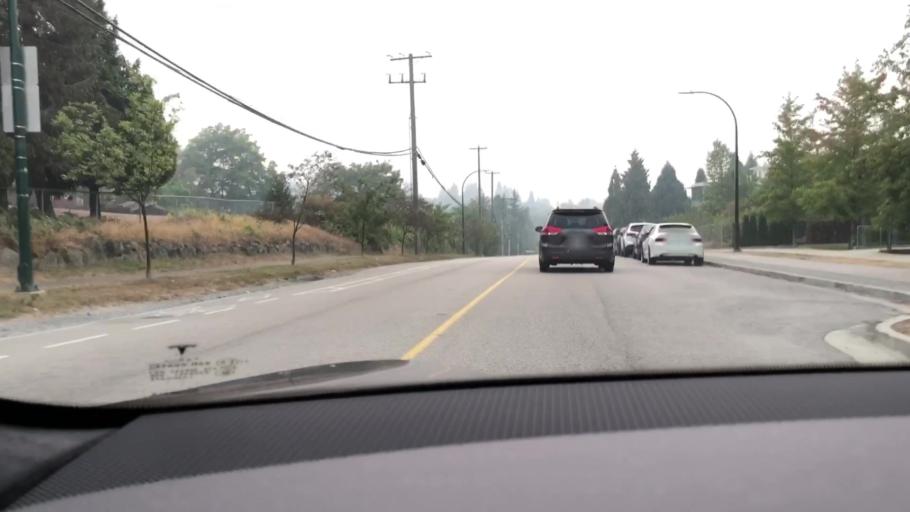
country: CA
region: British Columbia
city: Vancouver
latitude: 49.2412
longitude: -123.1209
